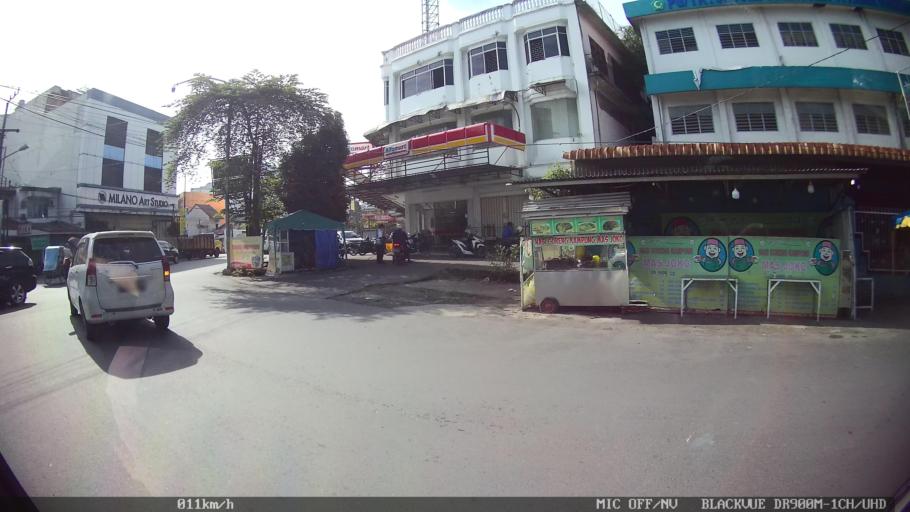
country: ID
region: North Sumatra
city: Medan
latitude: 3.5949
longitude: 98.6654
